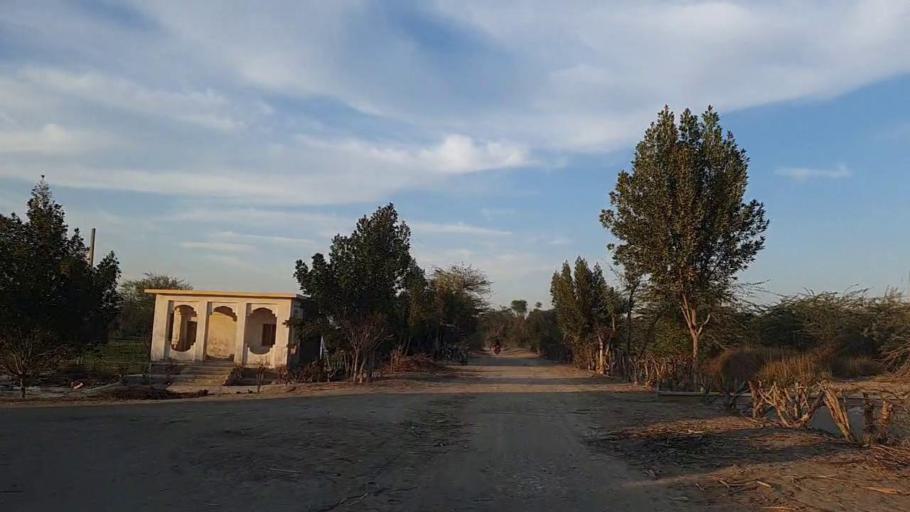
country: PK
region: Sindh
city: Bandhi
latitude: 26.6084
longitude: 68.3593
